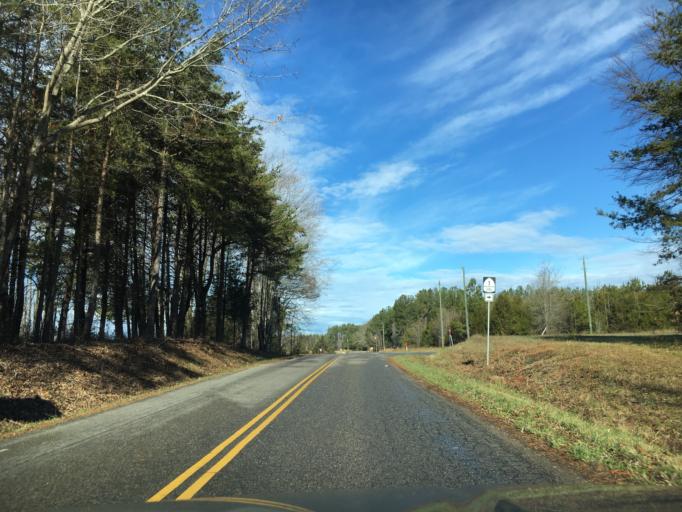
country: US
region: Virginia
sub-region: Amelia County
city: Amelia Court House
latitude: 37.3890
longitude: -78.1210
